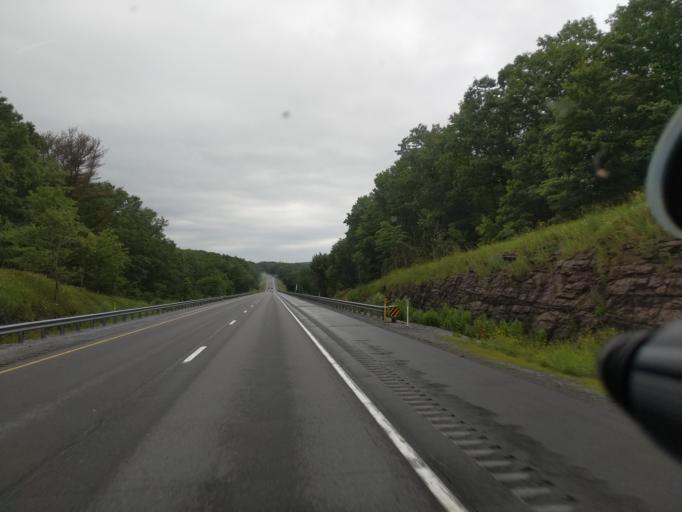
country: US
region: Pennsylvania
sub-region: Lycoming County
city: Jersey Shore
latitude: 41.0648
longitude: -77.2224
